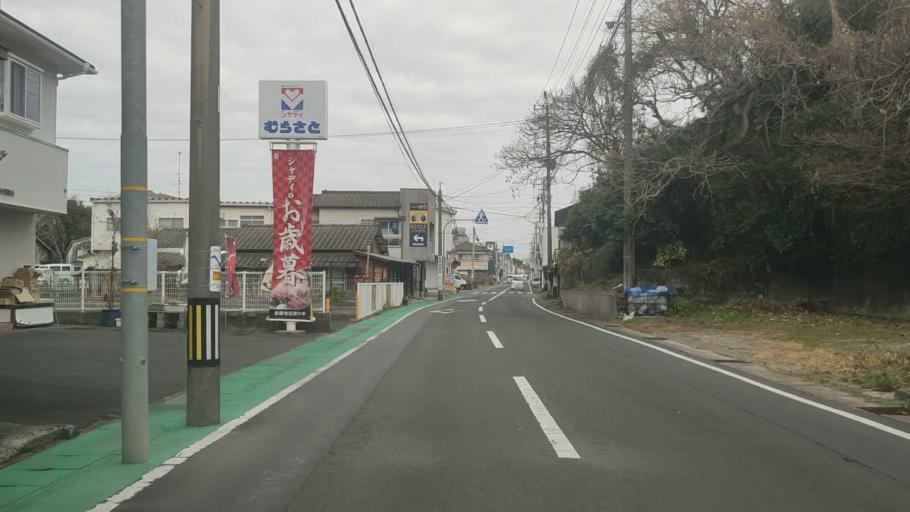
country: JP
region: Nagasaki
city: Shimabara
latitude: 32.7663
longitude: 130.3692
